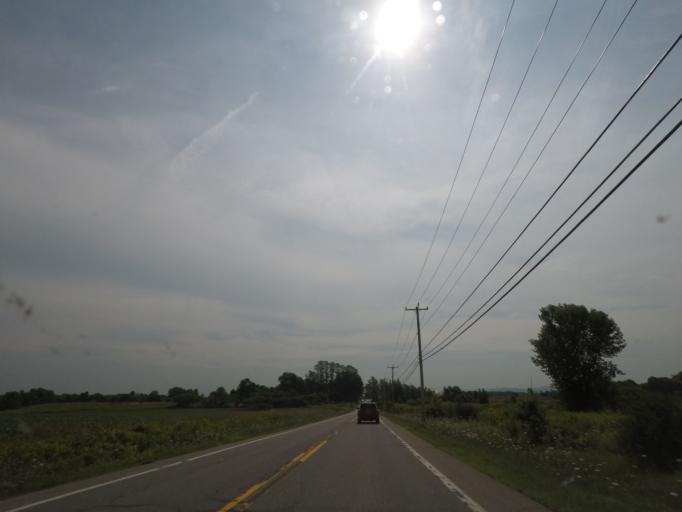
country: US
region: New York
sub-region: Saratoga County
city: Mechanicville
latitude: 42.8918
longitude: -73.7253
